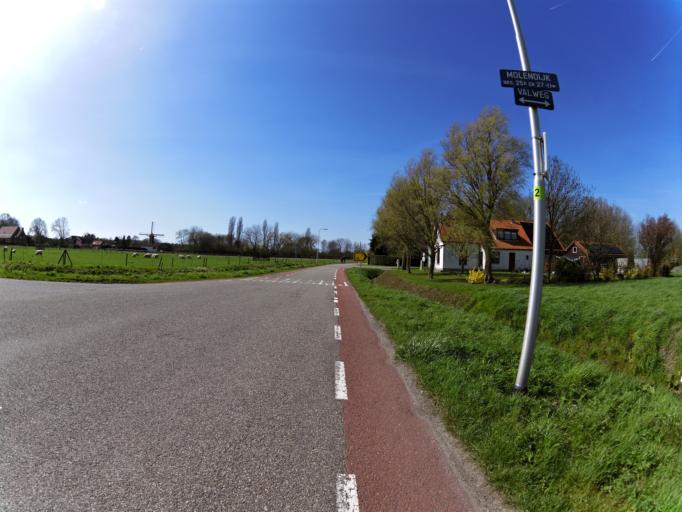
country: NL
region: South Holland
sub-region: Gemeente Brielle
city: Brielle
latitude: 51.9059
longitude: 4.1131
